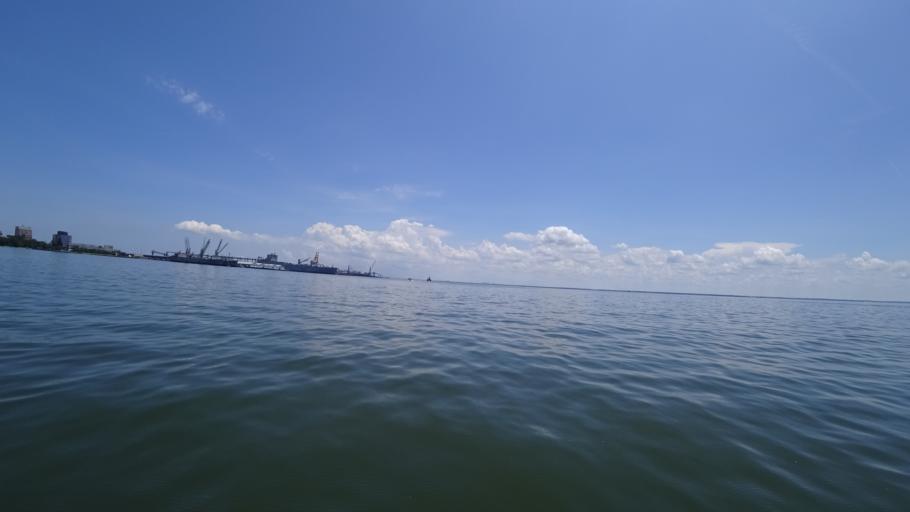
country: US
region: Virginia
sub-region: City of Newport News
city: Newport News
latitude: 36.9750
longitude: -76.4454
